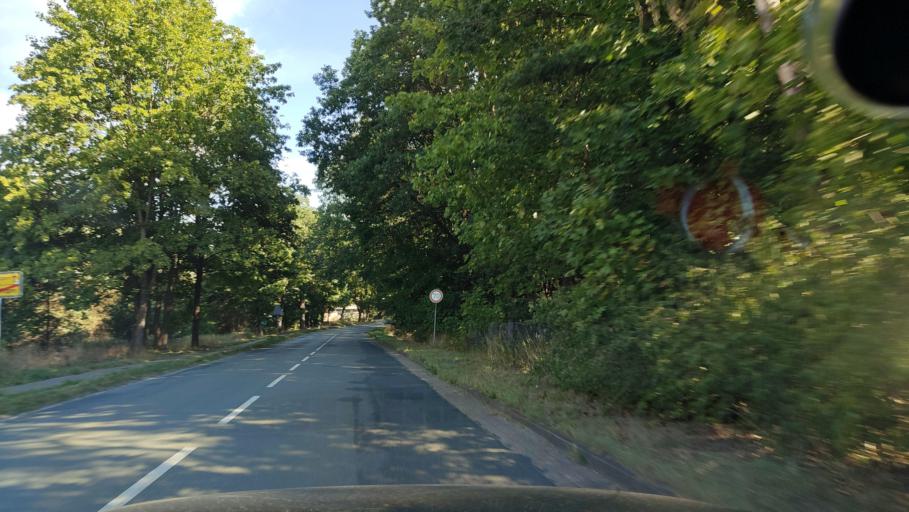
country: DE
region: Lower Saxony
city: Bomlitz
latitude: 52.8790
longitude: 9.6384
